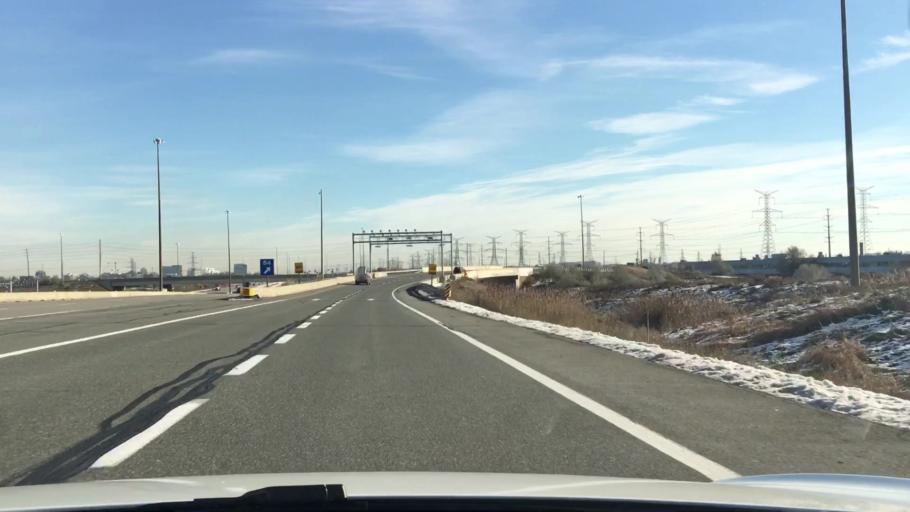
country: CA
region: Ontario
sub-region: York
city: Richmond Hill
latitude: 43.8398
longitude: -79.3613
